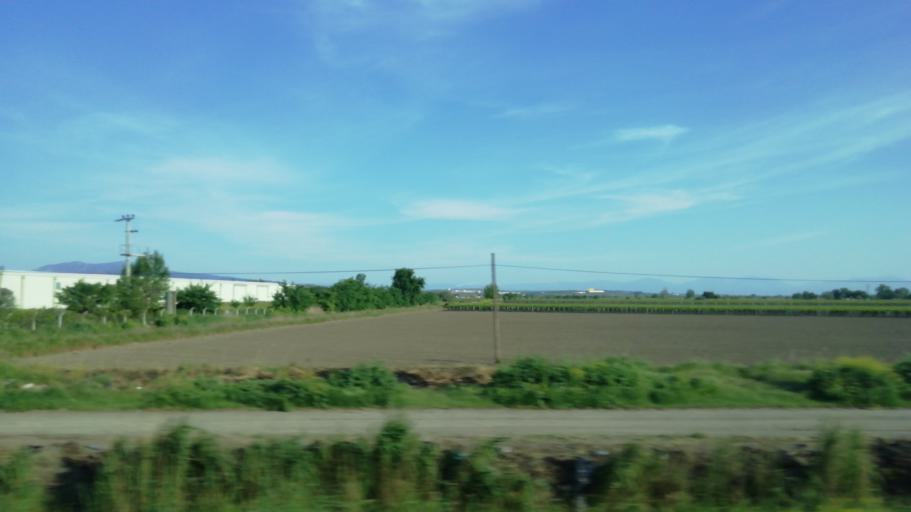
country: TR
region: Manisa
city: Saruhanli
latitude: 38.7262
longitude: 27.5732
